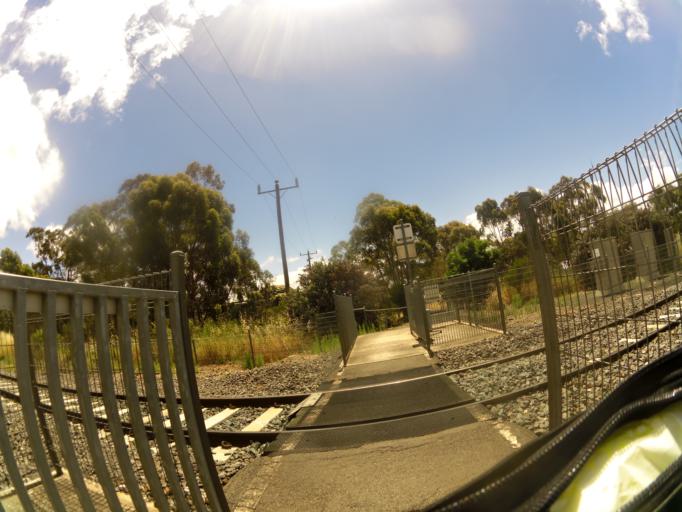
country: AU
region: Victoria
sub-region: Mount Alexander
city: Castlemaine
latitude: -37.0033
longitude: 144.2538
